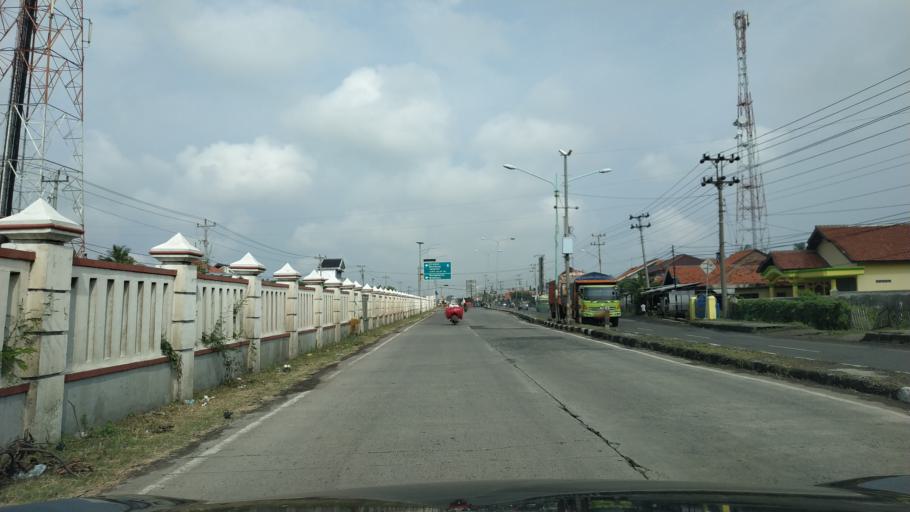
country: ID
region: Central Java
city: Ketanggungan
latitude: -6.8723
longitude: 108.8868
